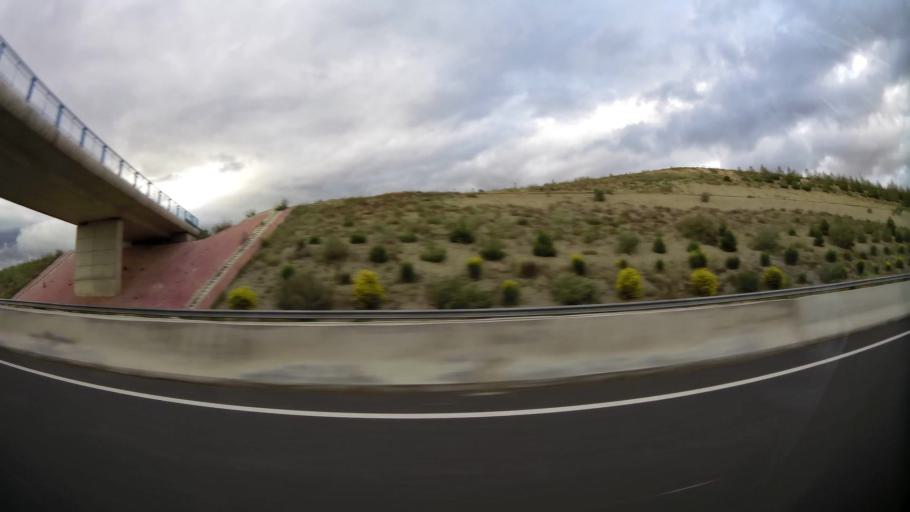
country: MA
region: Taza-Al Hoceima-Taounate
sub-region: Taza
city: Taza
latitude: 34.2538
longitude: -3.8800
